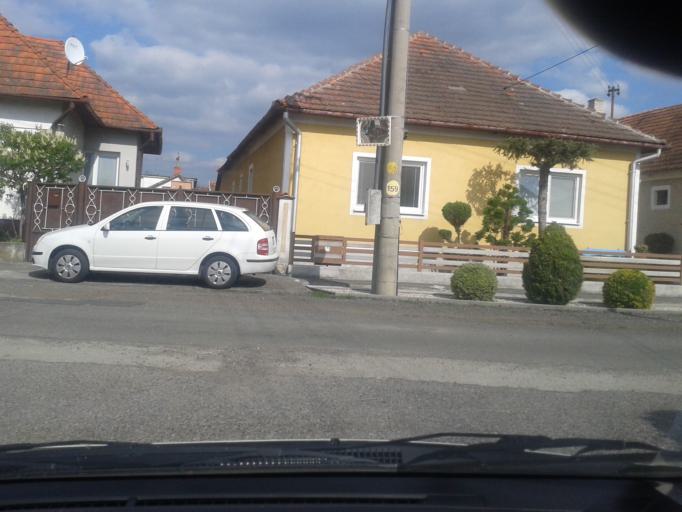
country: SK
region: Nitriansky
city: Tlmace
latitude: 48.2871
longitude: 18.6022
